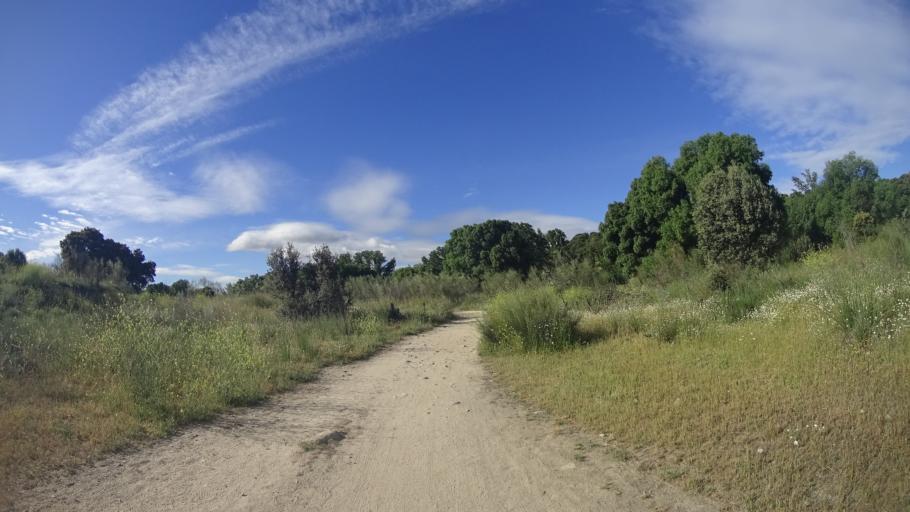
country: ES
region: Madrid
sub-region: Provincia de Madrid
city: Villanueva del Pardillo
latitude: 40.5154
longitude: -3.9413
